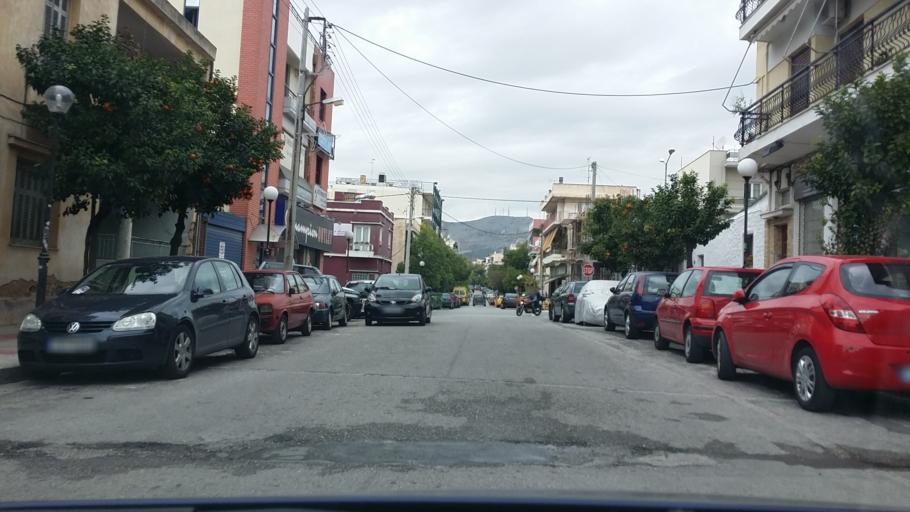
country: GR
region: Attica
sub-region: Nomarchia Athinas
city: Peristeri
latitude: 38.0122
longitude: 23.6893
